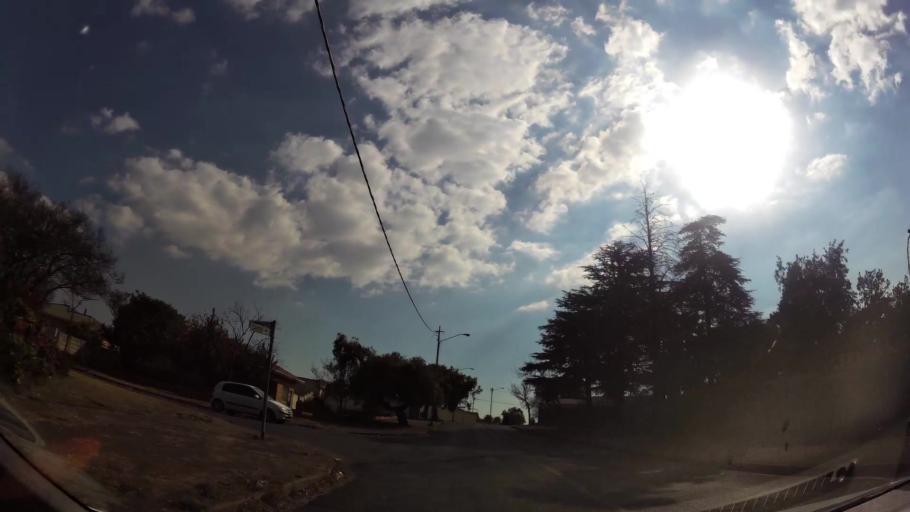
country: ZA
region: Gauteng
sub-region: Ekurhuleni Metropolitan Municipality
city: Germiston
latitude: -26.1773
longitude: 28.1678
